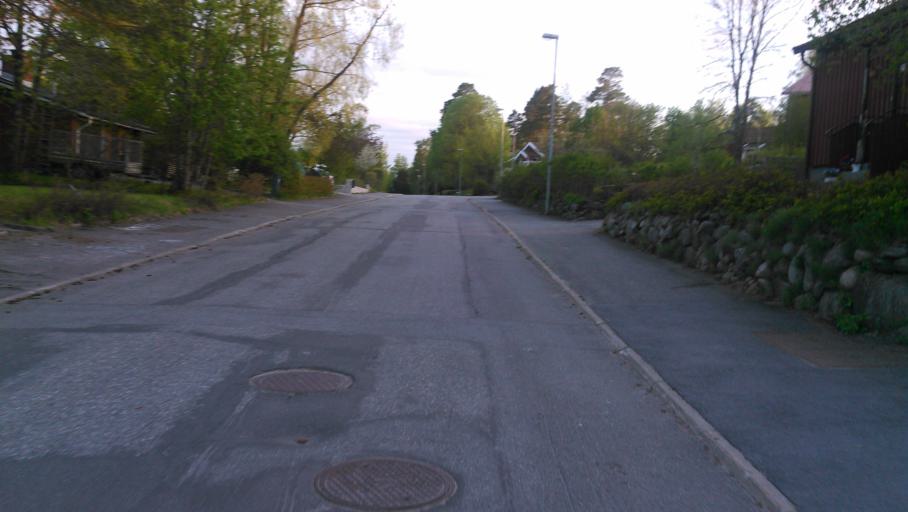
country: SE
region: Vaesterbotten
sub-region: Umea Kommun
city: Umea
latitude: 63.8317
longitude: 20.3101
